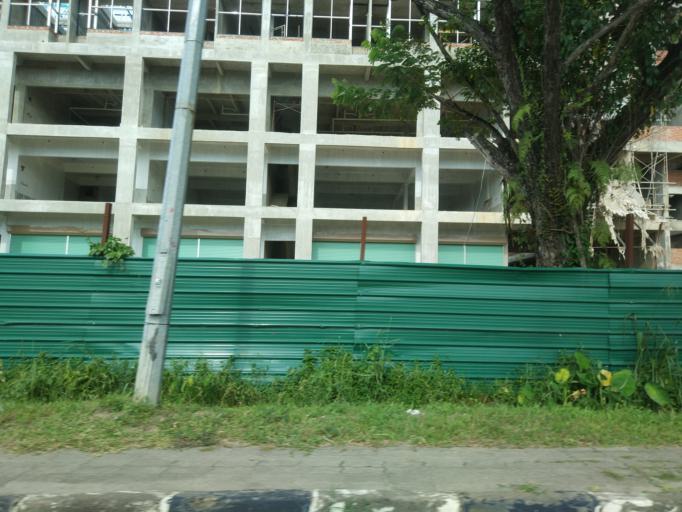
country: MY
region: Sabah
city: Beaufort
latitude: 5.0732
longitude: 115.5490
